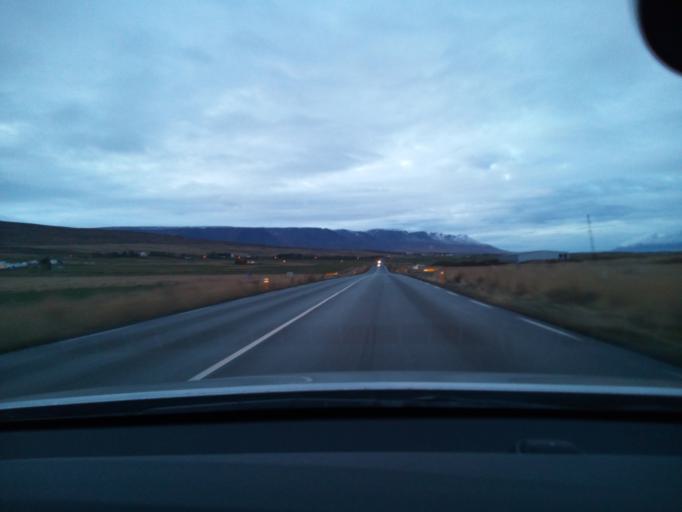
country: IS
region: Northeast
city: Akureyri
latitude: 65.7105
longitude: -18.1626
